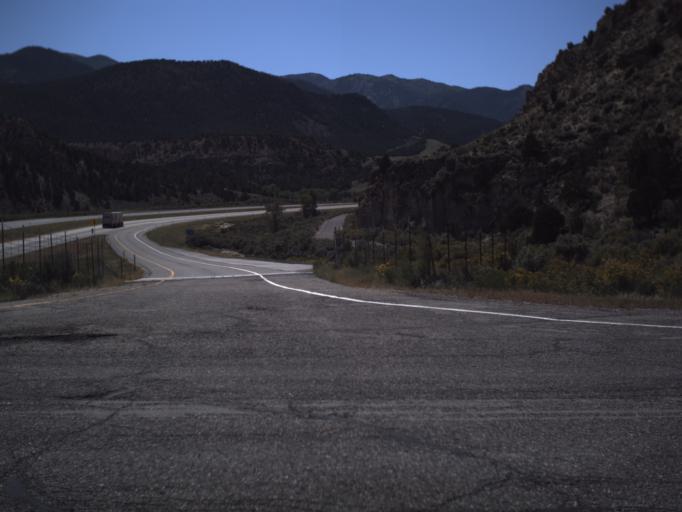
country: US
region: Utah
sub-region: Sevier County
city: Monroe
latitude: 38.5712
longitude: -112.3511
